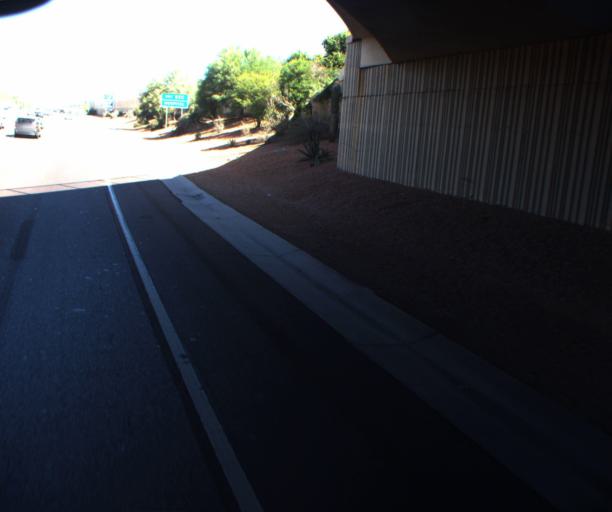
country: US
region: Arizona
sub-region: Maricopa County
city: San Carlos
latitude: 33.3640
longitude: -111.8937
